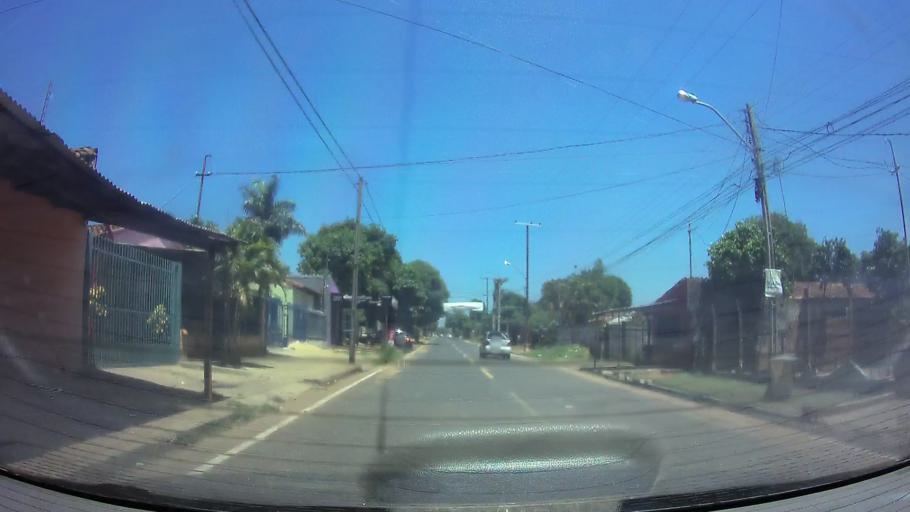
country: PY
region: Central
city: San Lorenzo
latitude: -25.3193
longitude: -57.4904
